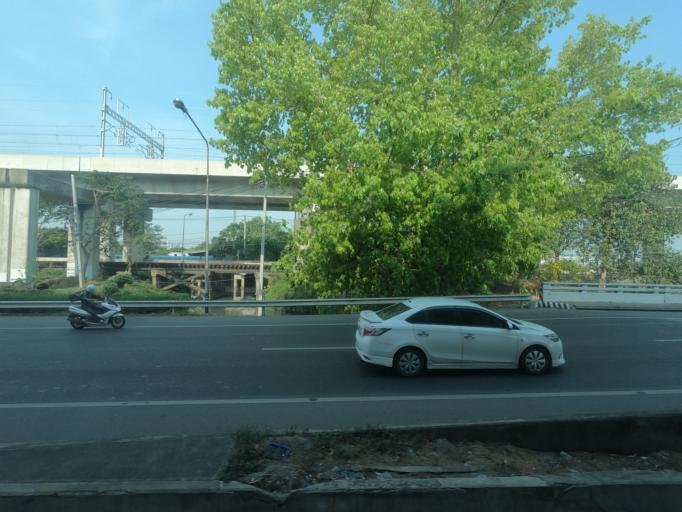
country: TH
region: Bangkok
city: Lak Si
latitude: 13.8739
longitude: 100.5613
